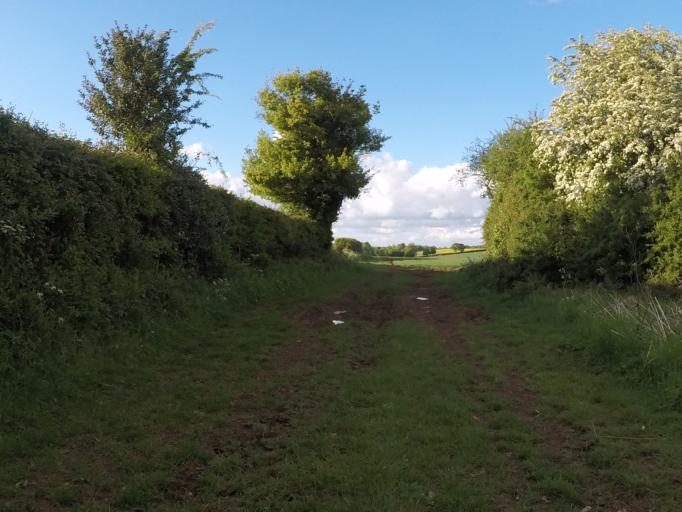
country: GB
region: England
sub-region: Oxfordshire
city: Stonesfield
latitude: 51.8603
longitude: -1.4554
